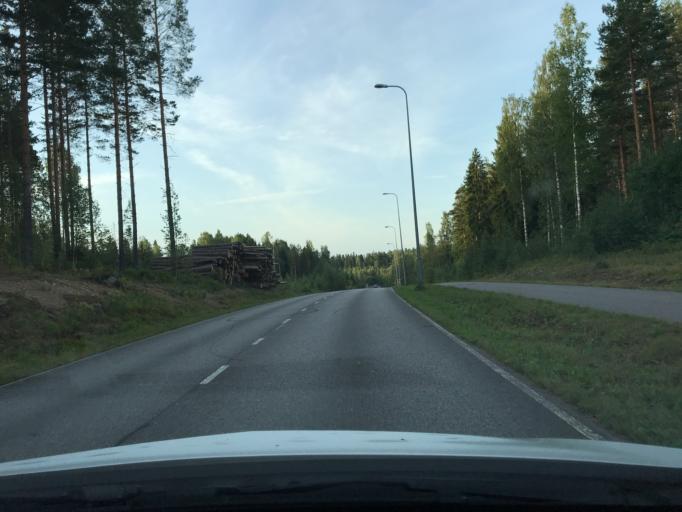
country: FI
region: Uusimaa
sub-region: Helsinki
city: Vihti
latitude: 60.4076
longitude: 24.4744
